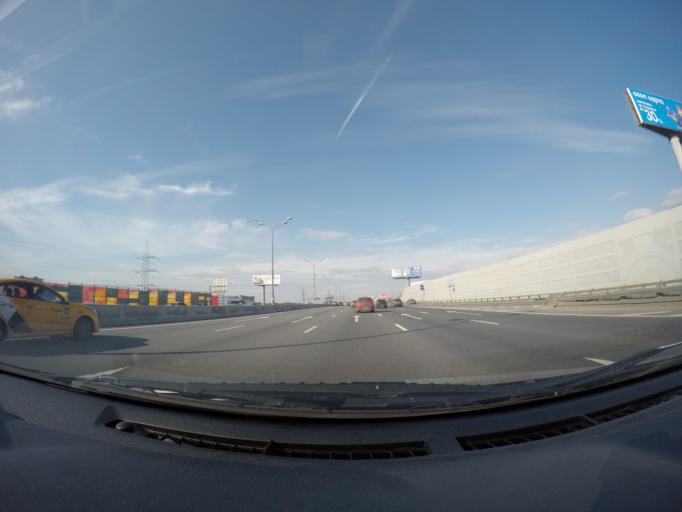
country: RU
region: Moscow
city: Yaroslavskiy
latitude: 55.8846
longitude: 37.7216
